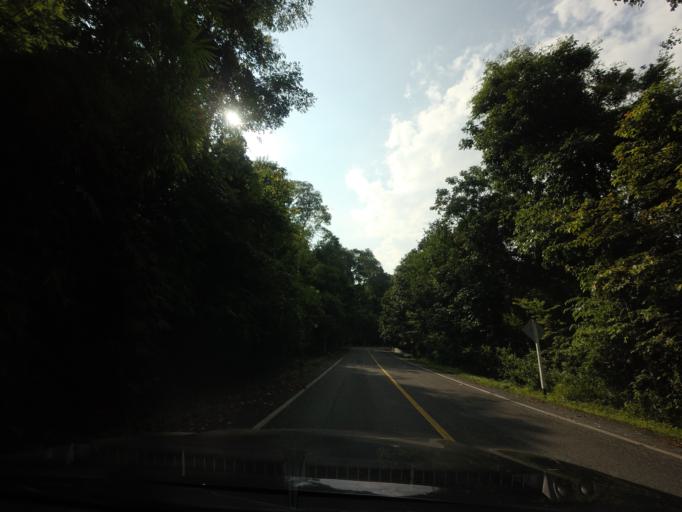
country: TH
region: Uttaradit
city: Ban Khok
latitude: 18.2726
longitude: 100.9735
